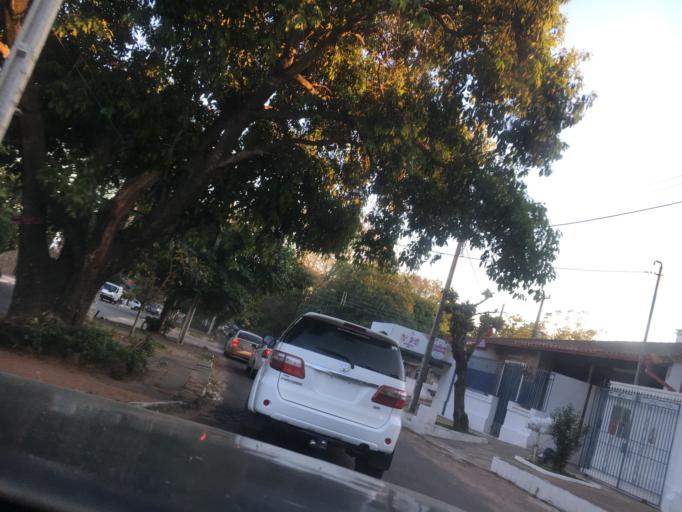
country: PY
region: Central
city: Lambare
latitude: -25.3289
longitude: -57.6098
